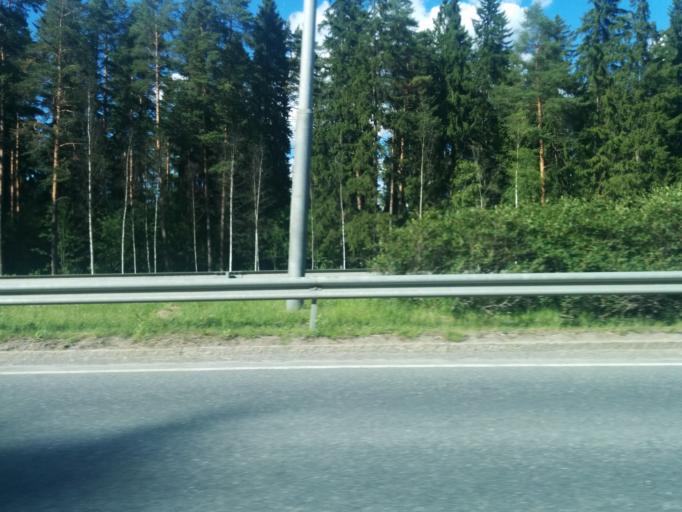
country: FI
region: Pirkanmaa
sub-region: Tampere
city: Tampere
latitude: 61.5010
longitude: 23.8715
